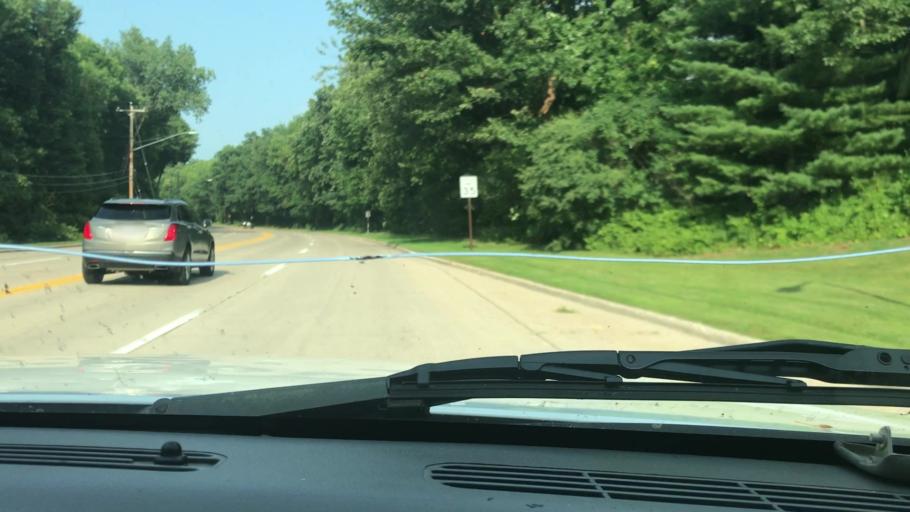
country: US
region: Wisconsin
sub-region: Brown County
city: Green Bay
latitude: 44.5308
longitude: -87.9344
